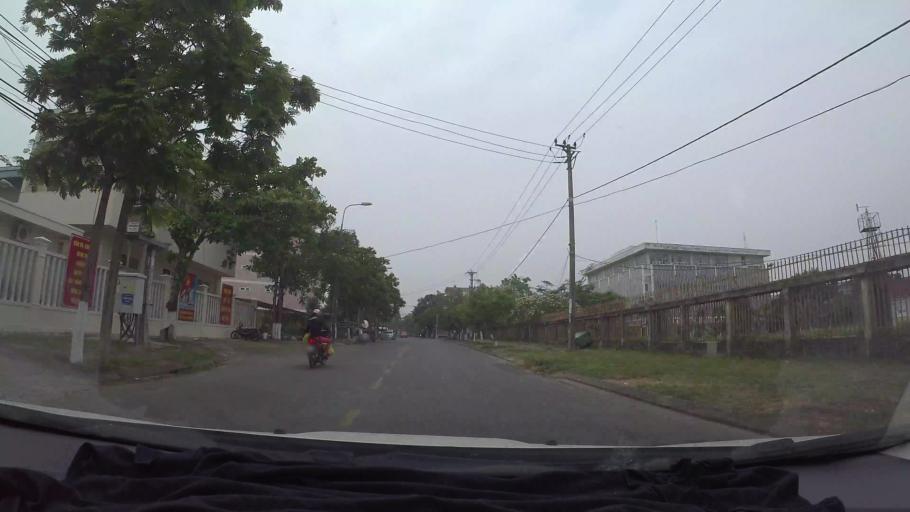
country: VN
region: Da Nang
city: Cam Le
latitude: 16.0430
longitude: 108.2069
